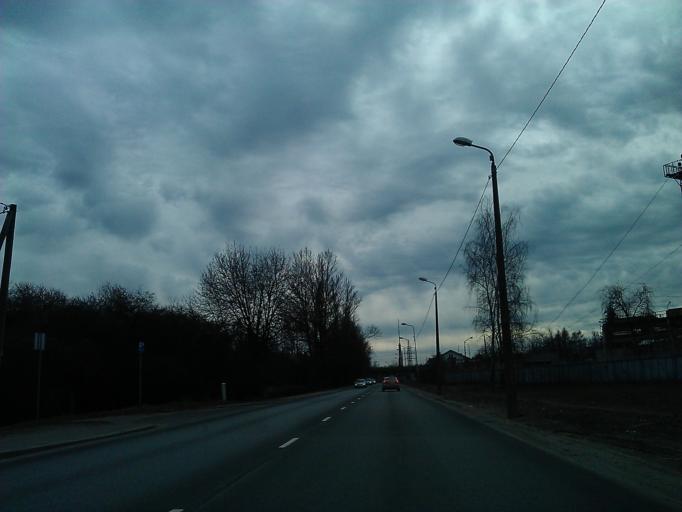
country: LV
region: Riga
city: Riga
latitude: 56.9553
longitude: 24.1649
